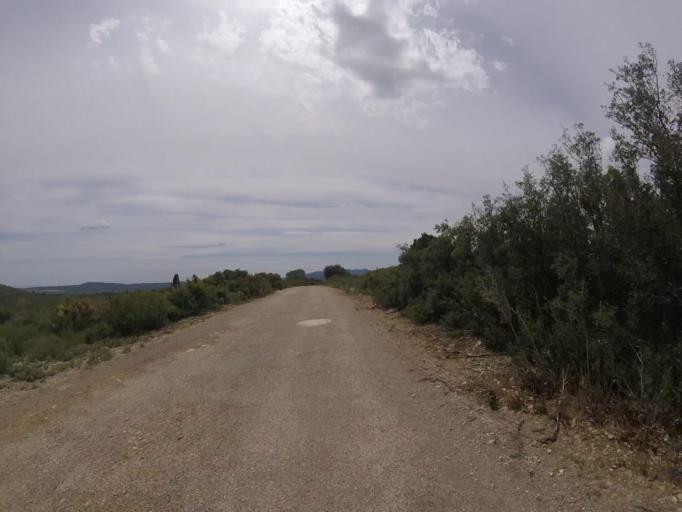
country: ES
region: Valencia
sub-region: Provincia de Castello
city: Sierra-Engarceran
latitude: 40.2345
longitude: -0.0260
